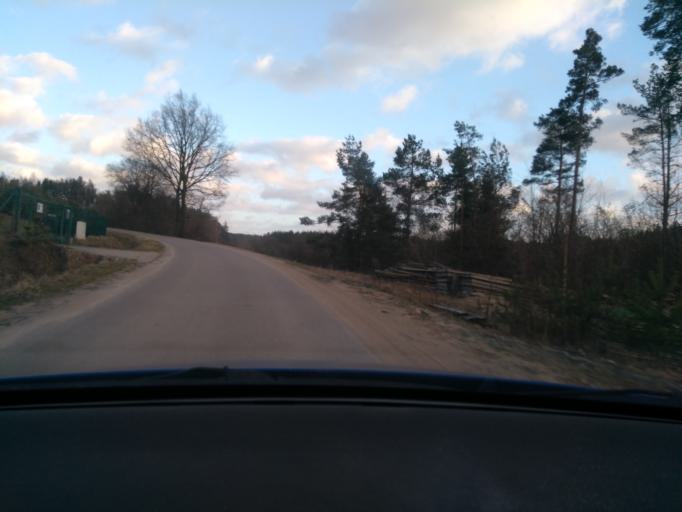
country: PL
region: Pomeranian Voivodeship
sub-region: Powiat kartuski
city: Przodkowo
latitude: 54.4137
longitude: 18.2506
